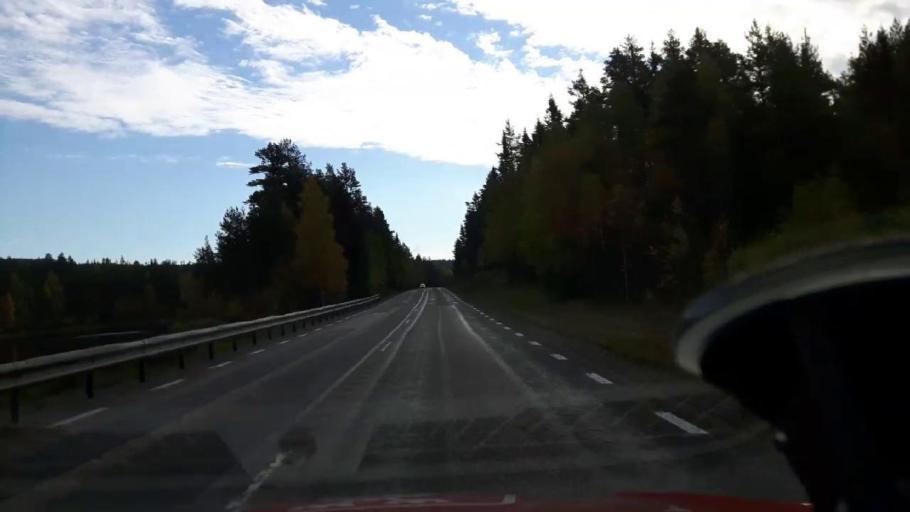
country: SE
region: Gaevleborg
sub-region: Ljusdals Kommun
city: Farila
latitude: 61.9749
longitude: 15.3351
